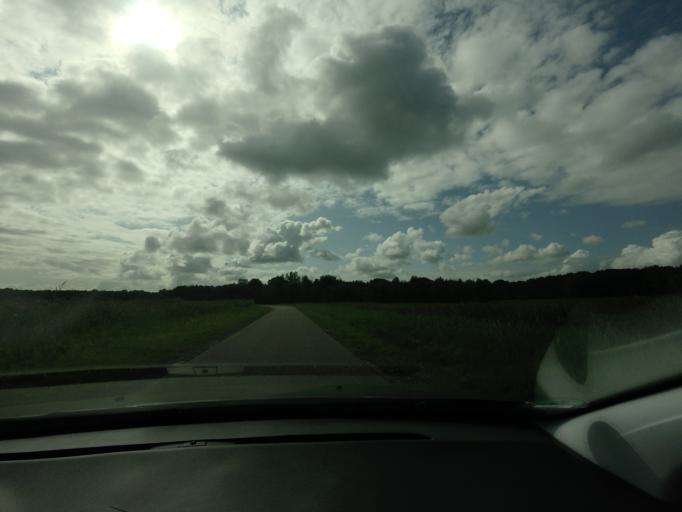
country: NL
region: North Holland
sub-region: Gemeente Hollands Kroon
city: Den Oever
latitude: 52.8914
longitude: 5.0724
